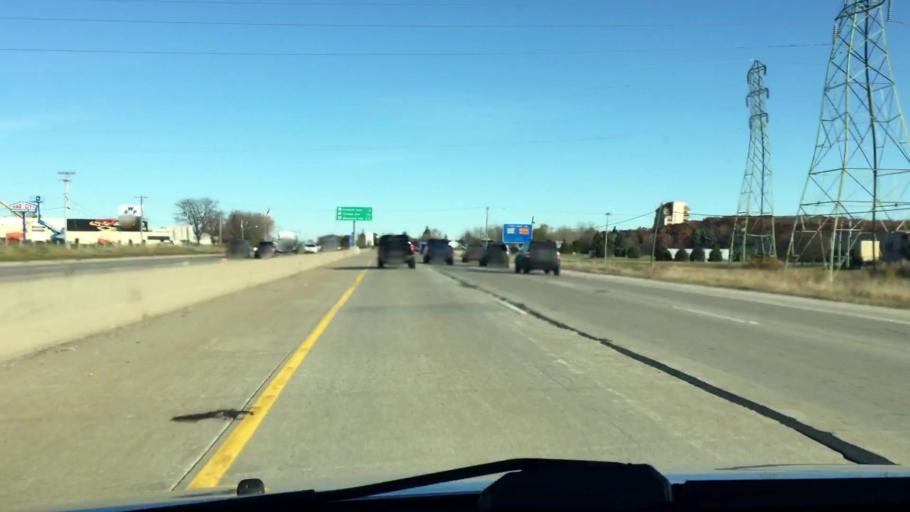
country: US
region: Wisconsin
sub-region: Winnebago County
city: Menasha
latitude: 44.2356
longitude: -88.4650
